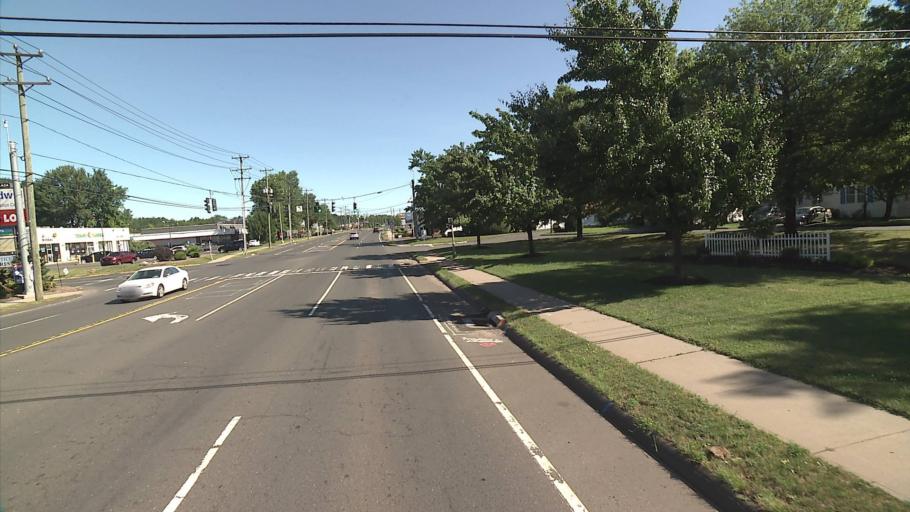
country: US
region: Connecticut
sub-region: Hartford County
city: Plainville
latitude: 41.6257
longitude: -72.8733
